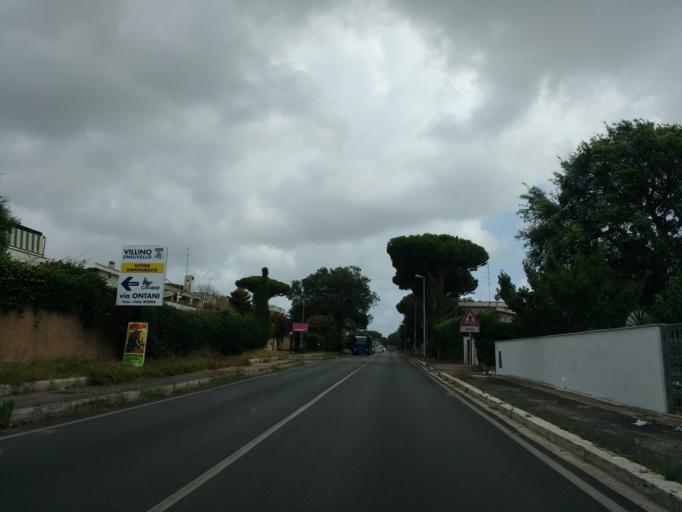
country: IT
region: Latium
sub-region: Citta metropolitana di Roma Capitale
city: Anzio
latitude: 41.4867
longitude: 12.5997
